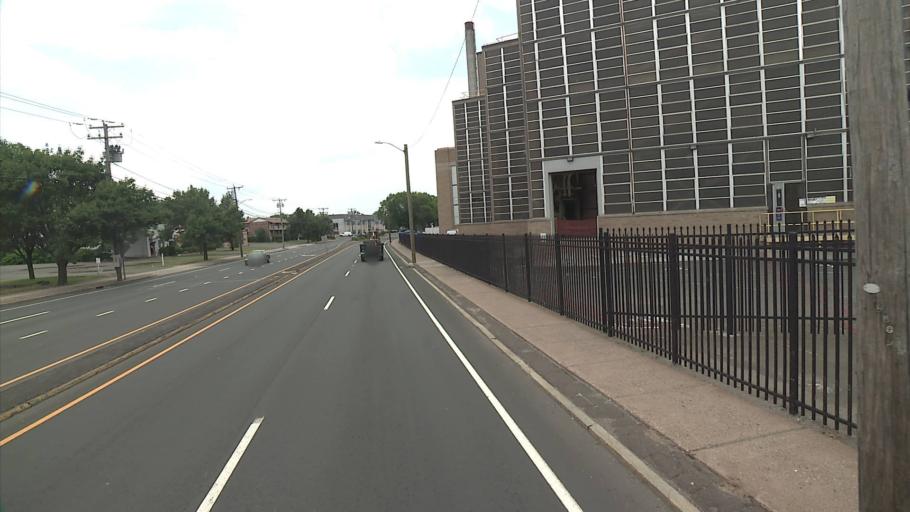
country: US
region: Connecticut
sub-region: Hartford County
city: Wethersfield
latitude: 41.7480
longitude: -72.6369
